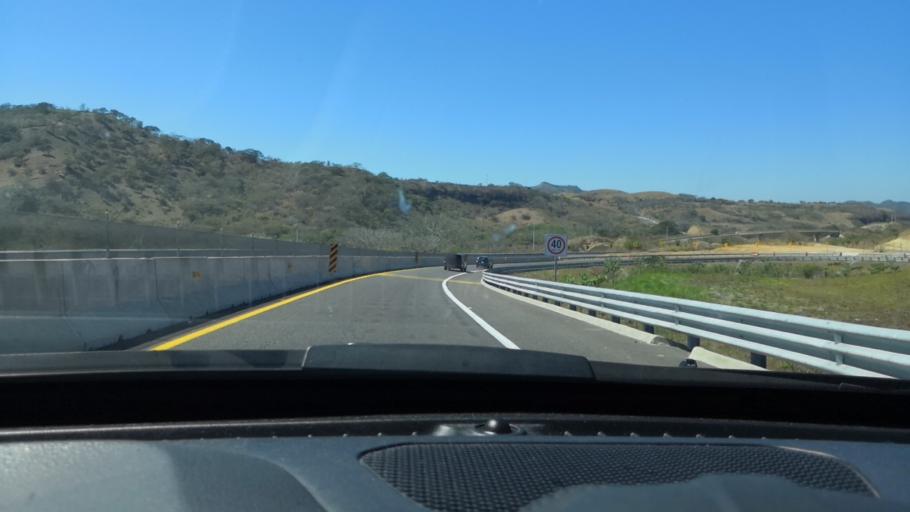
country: MX
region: Nayarit
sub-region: Compostela
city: Juan Escutia (Borbollon)
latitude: 21.1386
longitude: -104.9227
